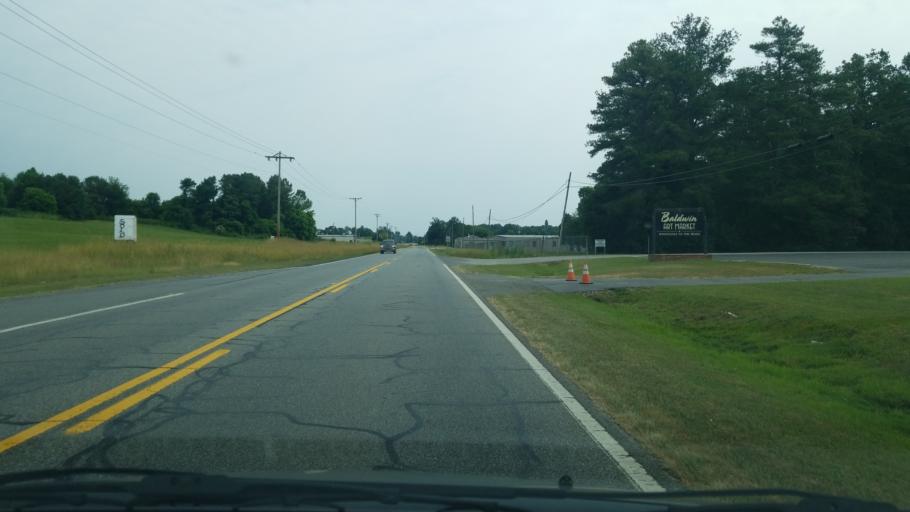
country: US
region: Georgia
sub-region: Catoosa County
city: Ringgold
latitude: 34.8648
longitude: -85.1439
